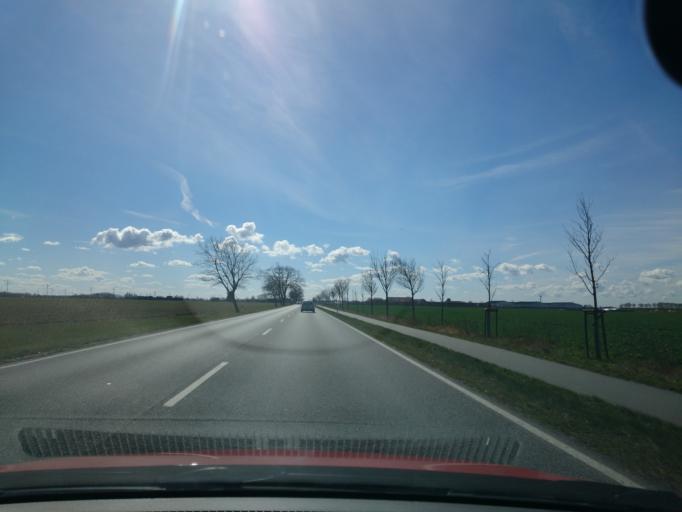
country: DE
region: Mecklenburg-Vorpommern
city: Rovershagen
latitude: 54.1689
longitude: 12.2388
